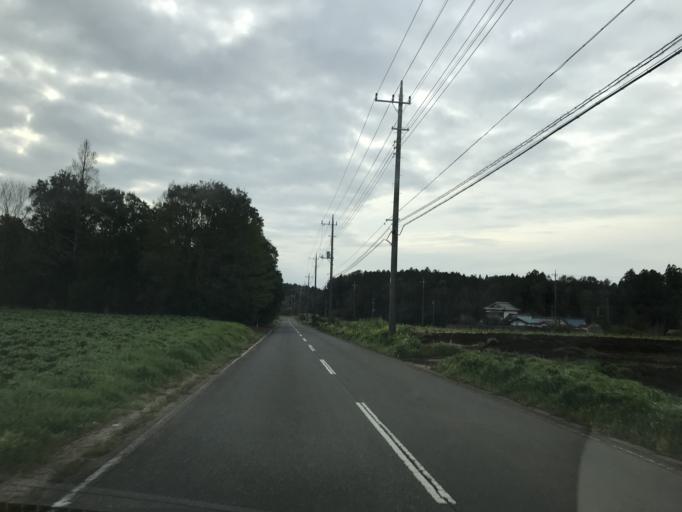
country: JP
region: Chiba
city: Omigawa
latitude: 35.8082
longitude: 140.5462
